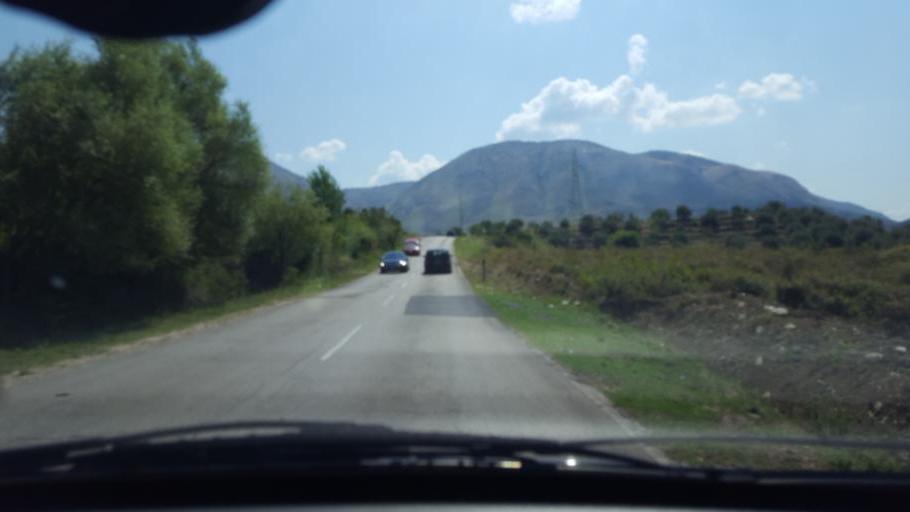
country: AL
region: Vlore
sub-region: Rrethi i Delvines
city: Mesopotam
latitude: 39.9116
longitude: 20.1147
